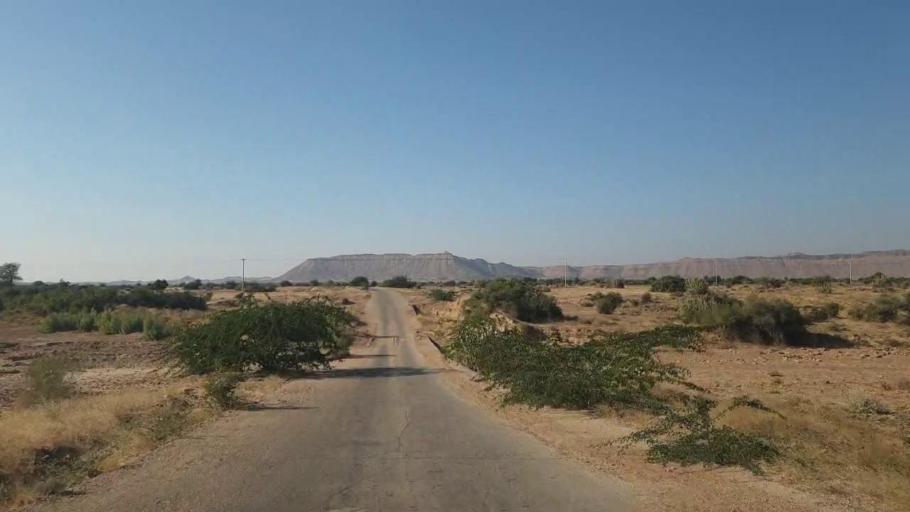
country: PK
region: Sindh
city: Malir Cantonment
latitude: 25.3875
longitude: 67.5277
